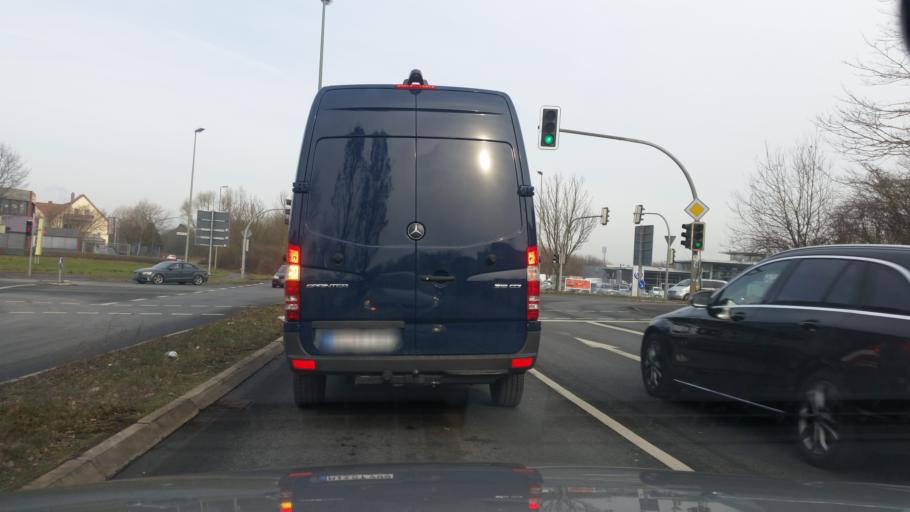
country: DE
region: North Rhine-Westphalia
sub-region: Regierungsbezirk Detmold
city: Oerlinghausen
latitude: 52.0053
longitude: 8.6122
